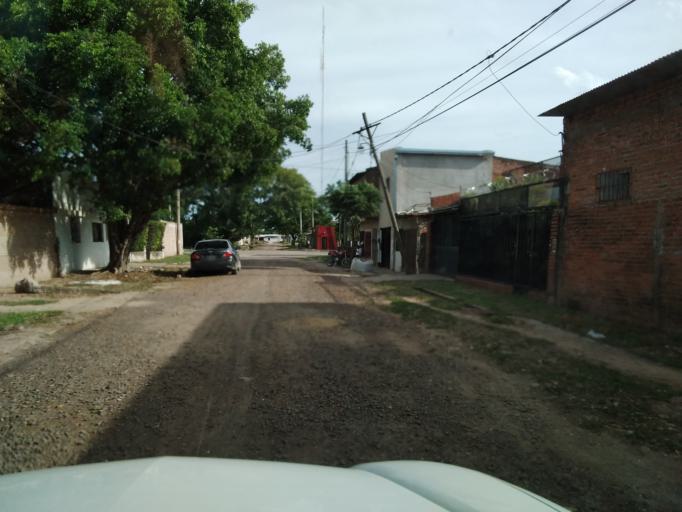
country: AR
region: Corrientes
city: Corrientes
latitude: -27.4874
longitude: -58.8468
